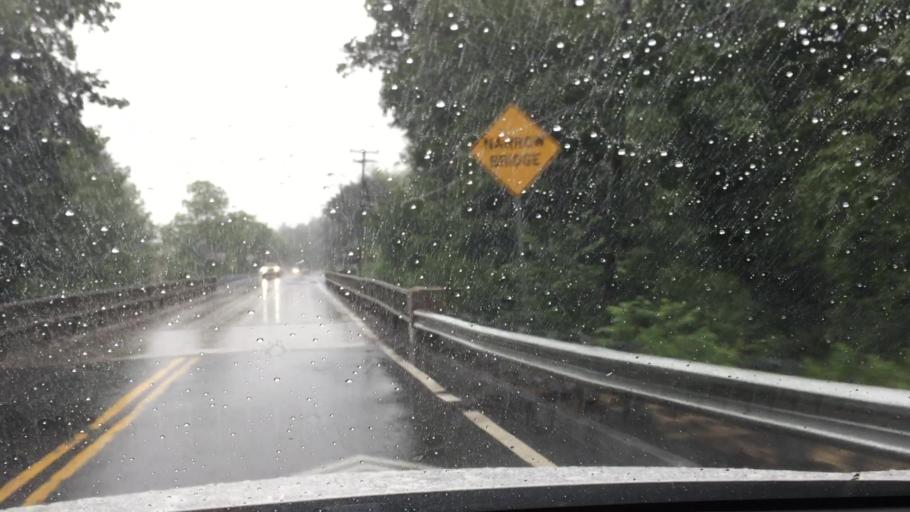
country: US
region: Massachusetts
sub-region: Berkshire County
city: Dalton
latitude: 42.4707
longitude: -73.1687
